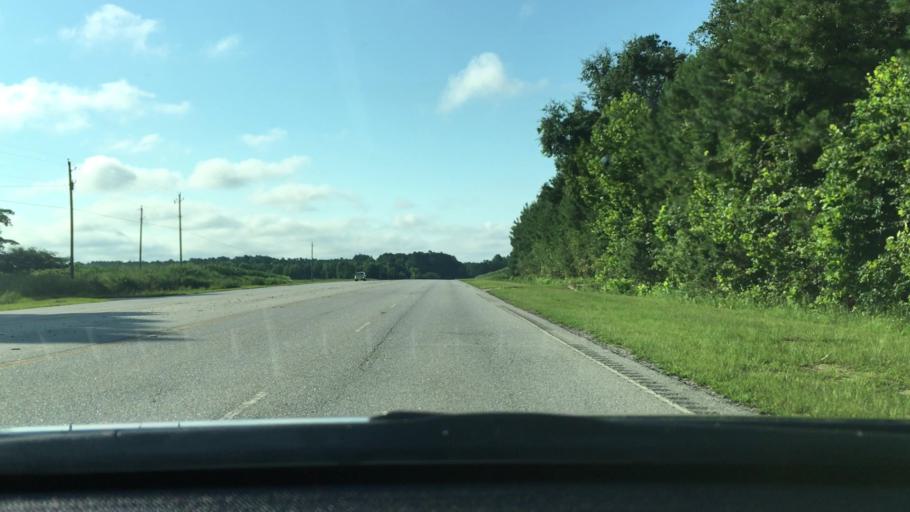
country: US
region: South Carolina
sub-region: Clarendon County
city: Manning
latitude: 33.7799
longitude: -80.2450
